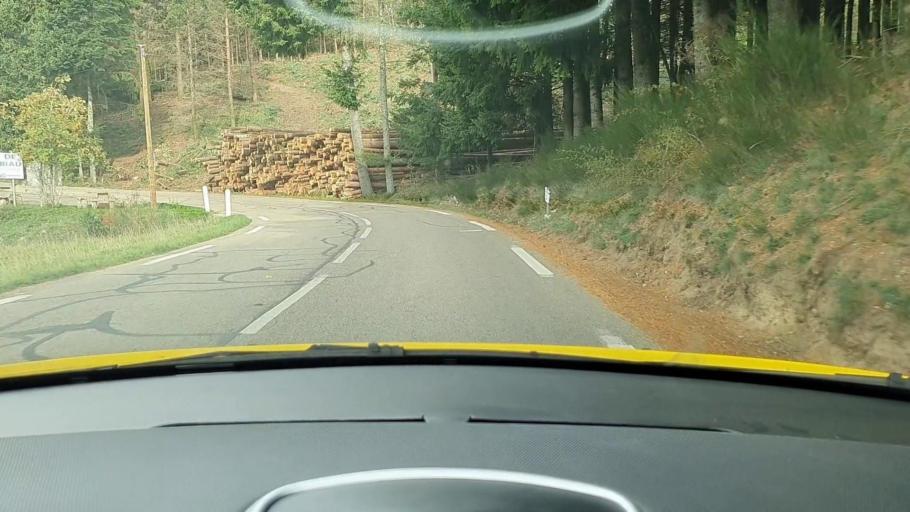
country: FR
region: Languedoc-Roussillon
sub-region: Departement de la Lozere
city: Meyrueis
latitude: 44.1220
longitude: 3.4822
